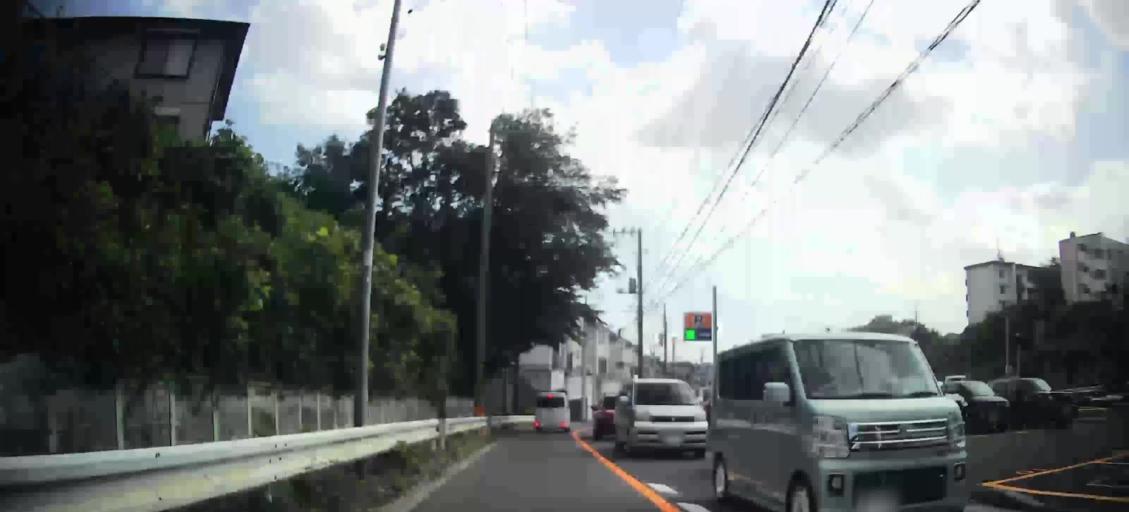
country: JP
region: Kanagawa
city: Yokohama
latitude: 35.4801
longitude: 139.5770
